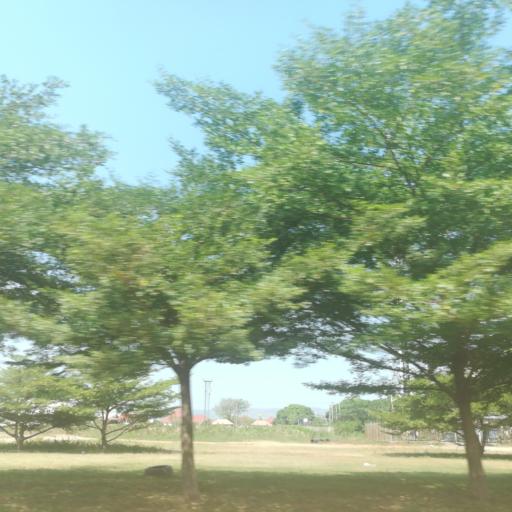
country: NG
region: Abuja Federal Capital Territory
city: Abuja
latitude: 9.0780
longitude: 7.4320
